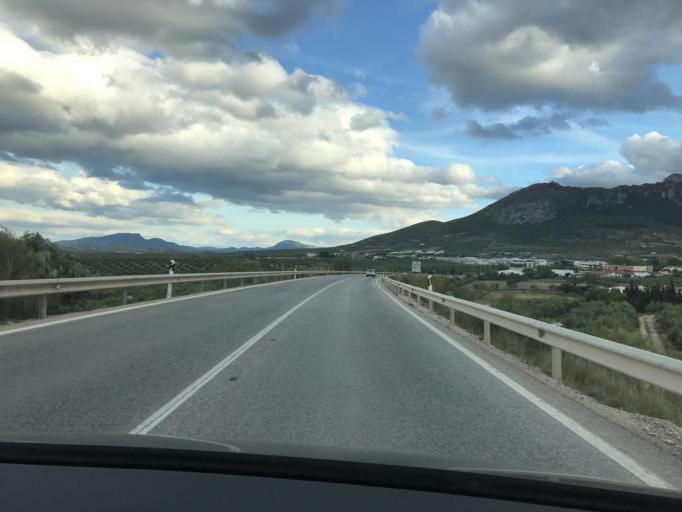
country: ES
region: Andalusia
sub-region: Provincia de Jaen
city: Jodar
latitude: 37.8471
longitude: -3.3453
